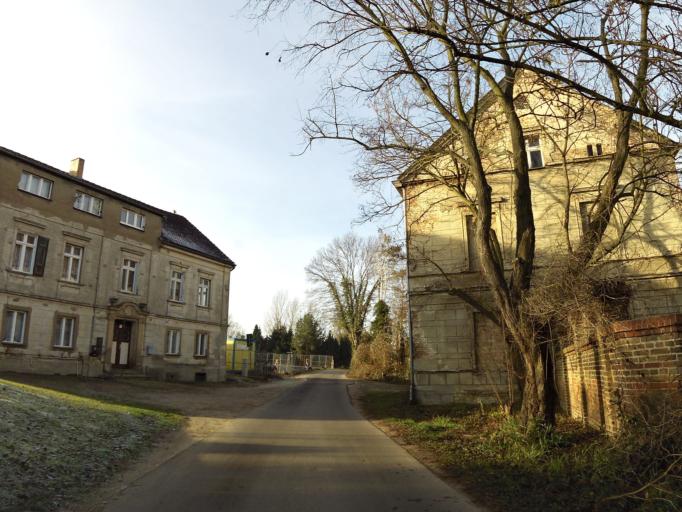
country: DE
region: Brandenburg
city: Werder
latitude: 52.3551
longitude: 12.9216
